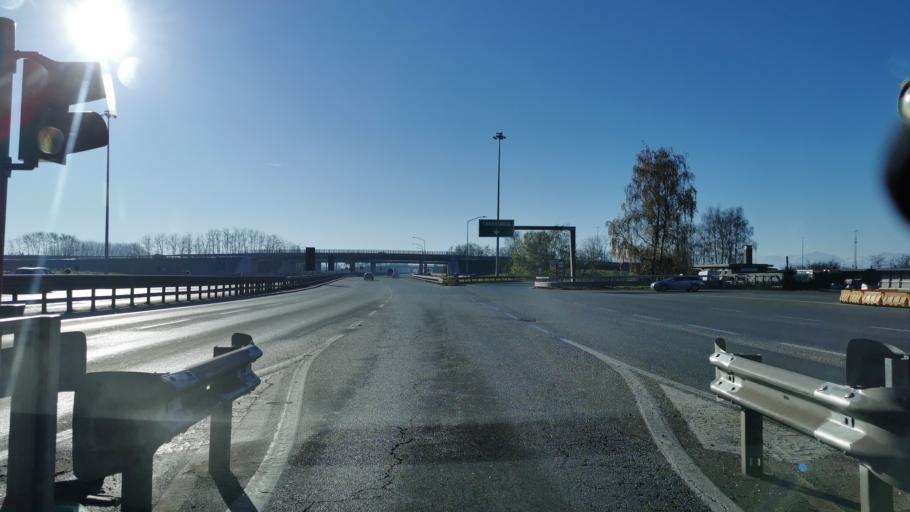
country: IT
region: Piedmont
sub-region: Provincia di Torino
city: Carmagnola
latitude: 44.8544
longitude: 7.7495
